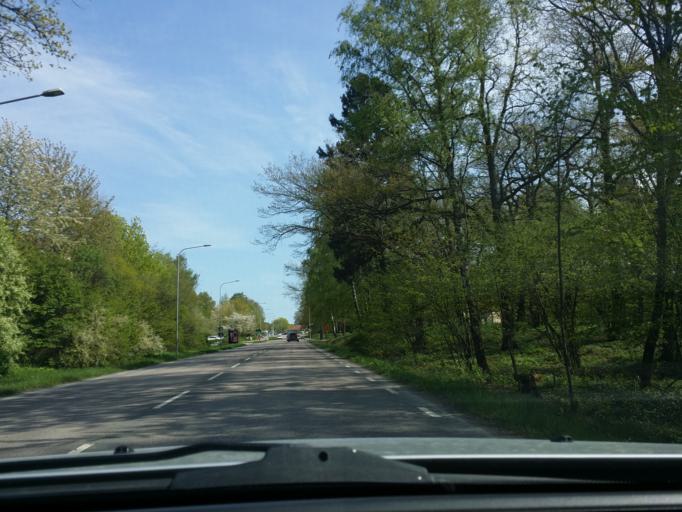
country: SE
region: Vaestmanland
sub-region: Vasteras
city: Vasteras
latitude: 59.6066
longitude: 16.5768
